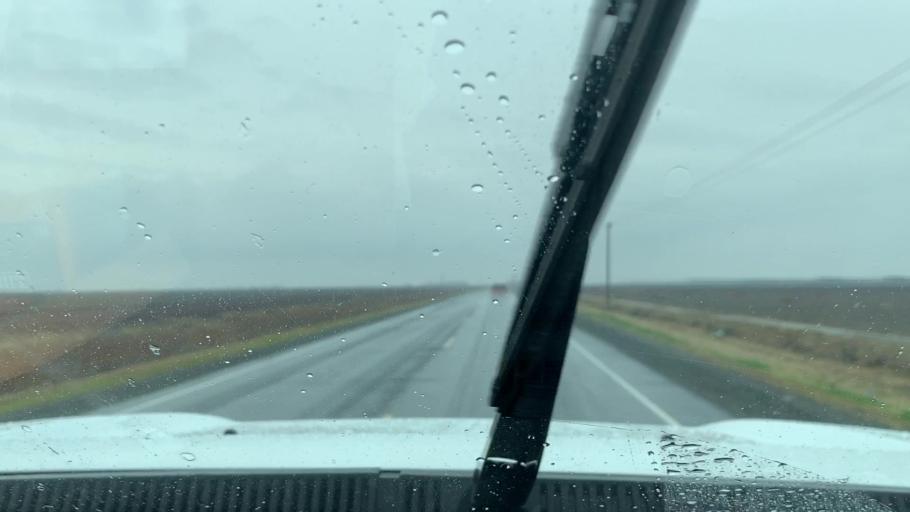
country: US
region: California
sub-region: Tulare County
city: Alpaugh
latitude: 35.9293
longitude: -119.4329
